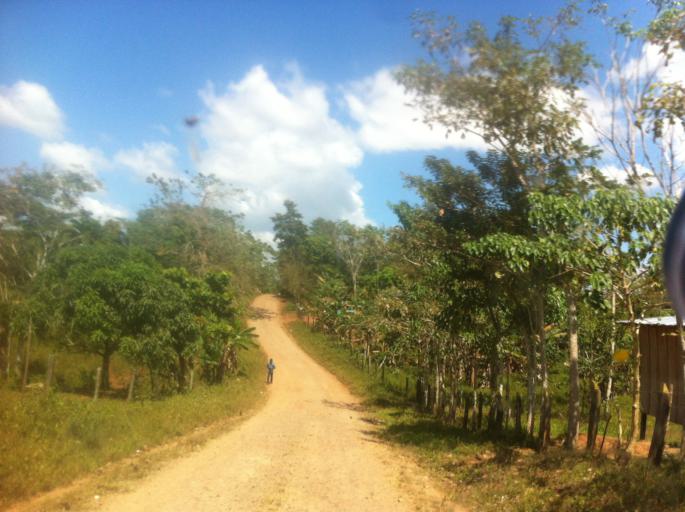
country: CR
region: Alajuela
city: Los Chiles
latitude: 11.2367
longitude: -84.4828
